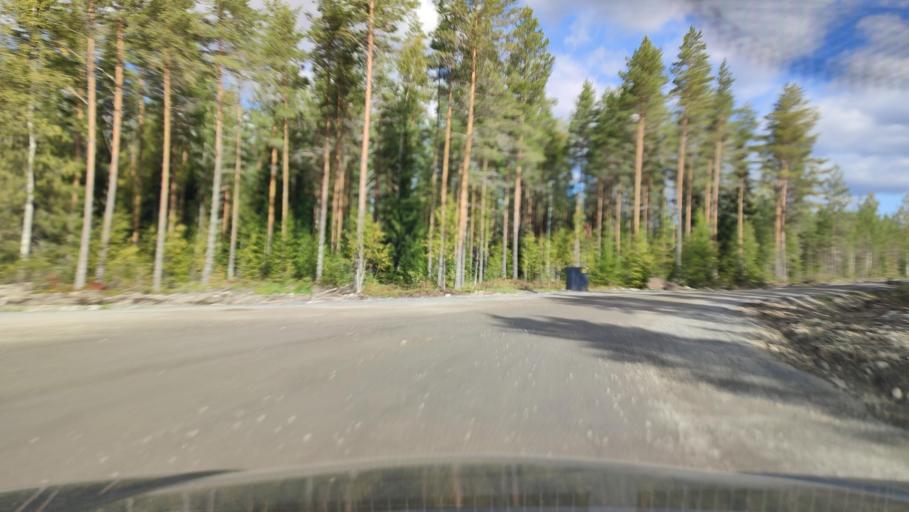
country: FI
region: Southern Ostrobothnia
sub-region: Suupohja
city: Karijoki
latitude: 62.2031
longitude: 21.5873
